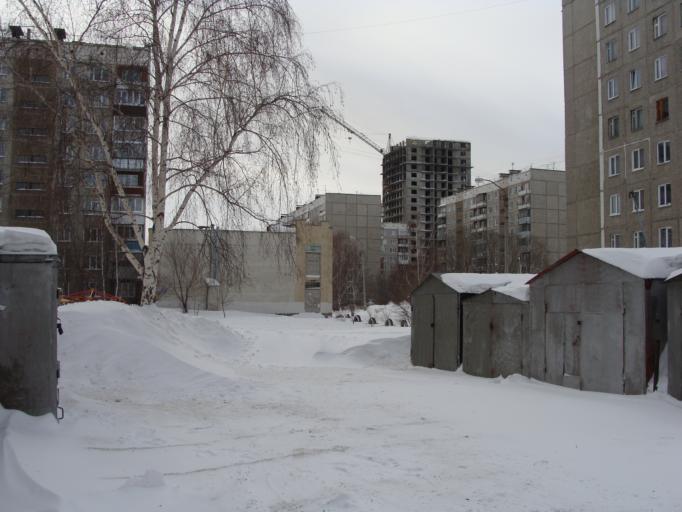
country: RU
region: Altai Krai
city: Novosilikatnyy
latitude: 53.3603
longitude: 83.6797
